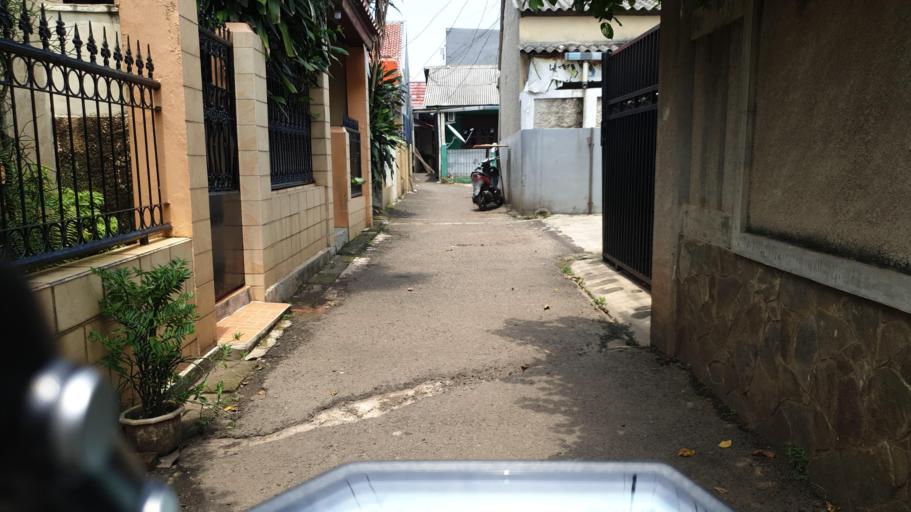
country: ID
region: West Java
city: Depok
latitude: -6.3317
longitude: 106.8301
